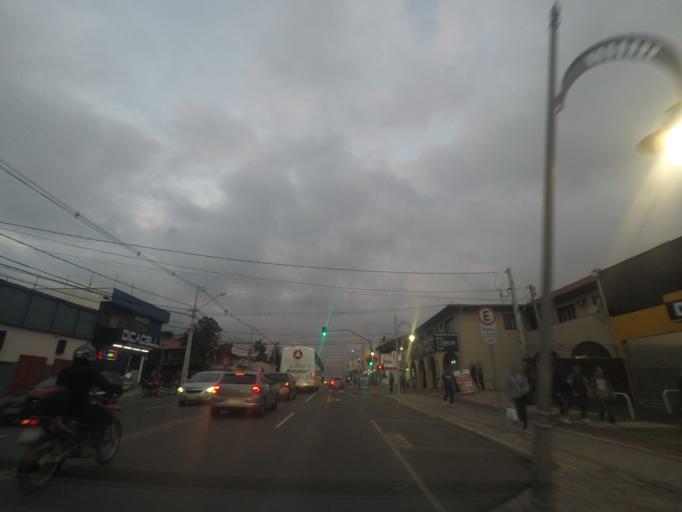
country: BR
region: Parana
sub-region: Almirante Tamandare
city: Almirante Tamandare
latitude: -25.3952
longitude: -49.3474
